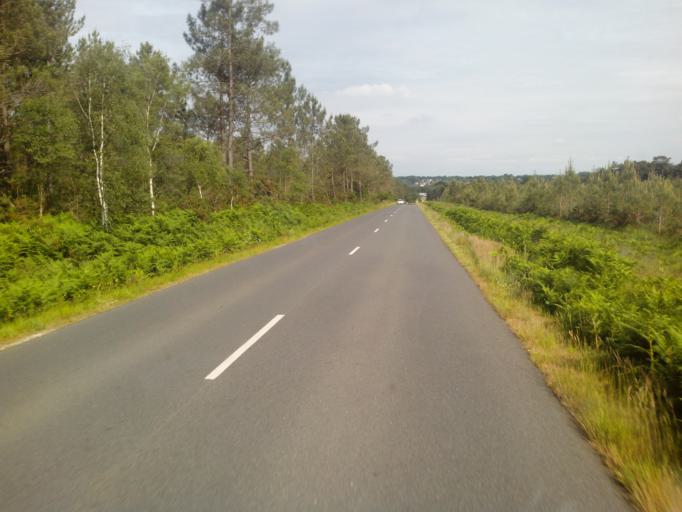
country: FR
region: Brittany
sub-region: Departement d'Ille-et-Vilaine
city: Plelan-le-Grand
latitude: 48.0092
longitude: -2.1265
